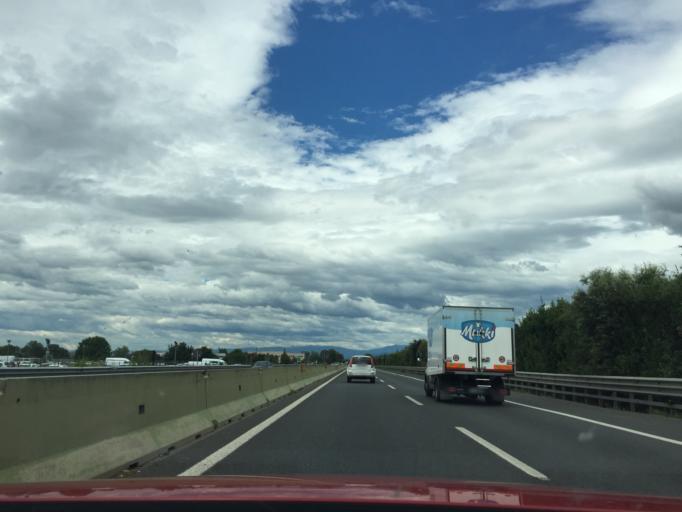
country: IT
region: Tuscany
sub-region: Province of Florence
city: Sesto Fiorentino
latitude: 43.8027
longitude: 11.1983
